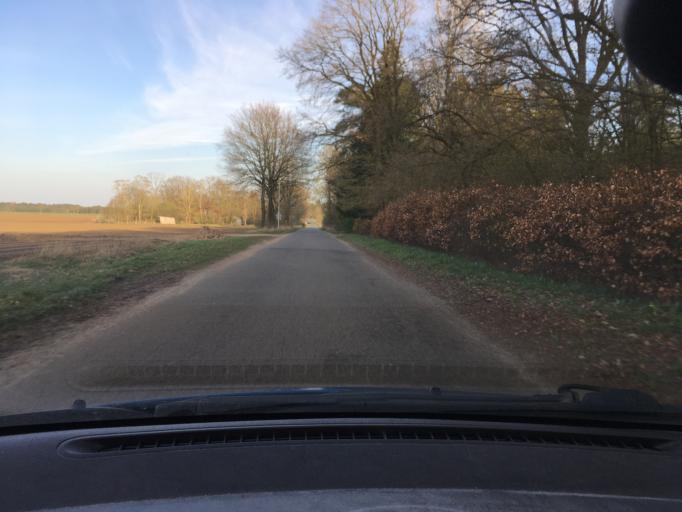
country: DE
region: Lower Saxony
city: Bispingen
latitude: 53.1096
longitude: 10.0226
